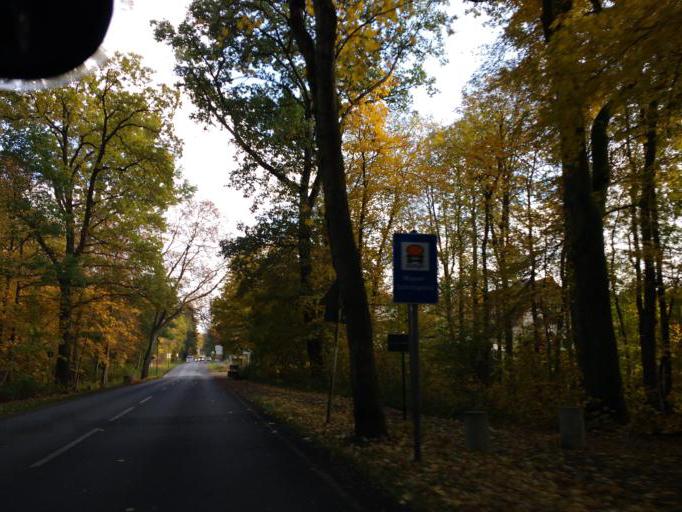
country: DE
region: Brandenburg
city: Petershagen
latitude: 52.5580
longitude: 13.8227
